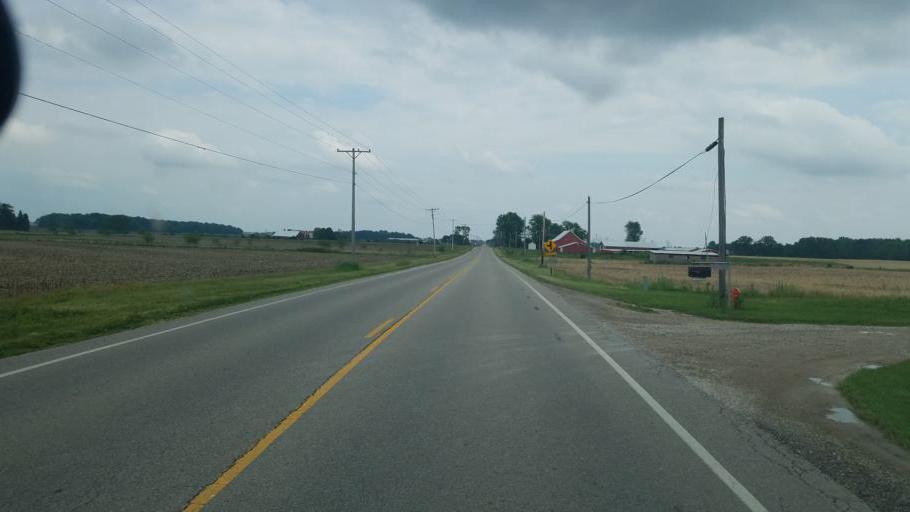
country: US
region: Ohio
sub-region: Union County
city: New California
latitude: 40.1974
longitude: -83.2994
